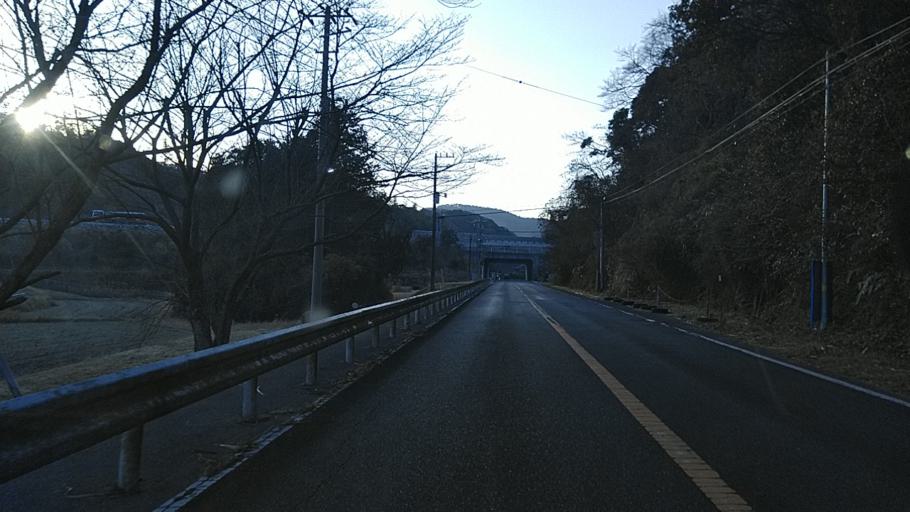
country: JP
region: Chiba
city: Kimitsu
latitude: 35.2807
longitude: 139.9234
